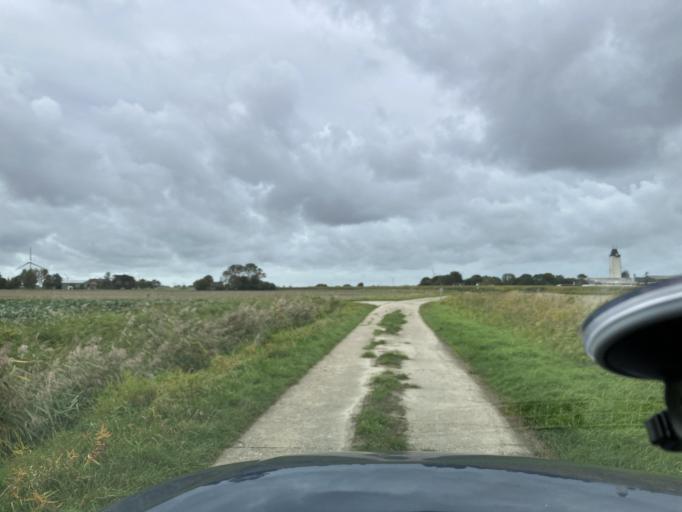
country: DE
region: Schleswig-Holstein
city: Norderwohrden
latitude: 54.2138
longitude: 9.0158
